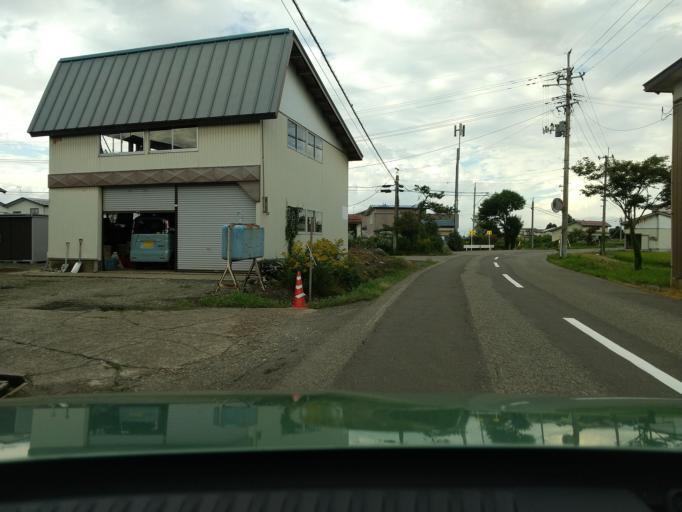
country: JP
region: Akita
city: Yokotemachi
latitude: 39.2902
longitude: 140.4813
